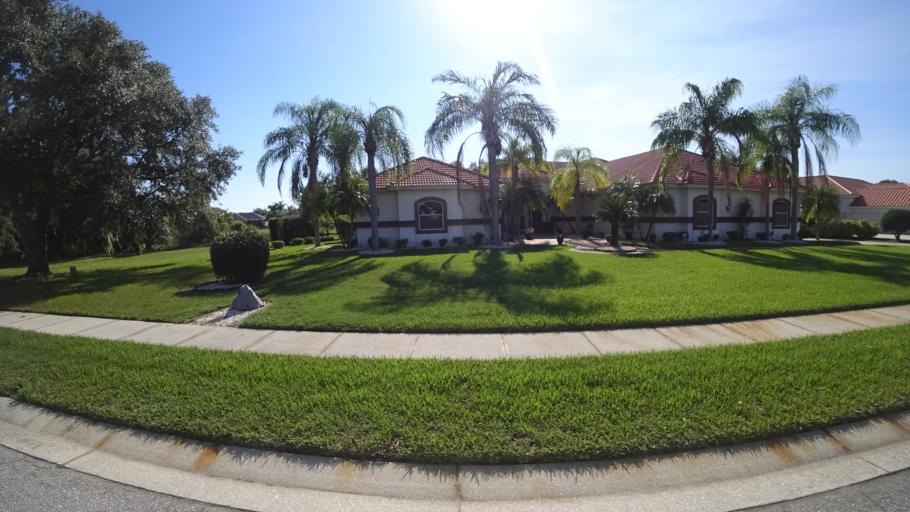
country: US
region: Florida
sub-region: Sarasota County
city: The Meadows
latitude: 27.4163
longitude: -82.4392
